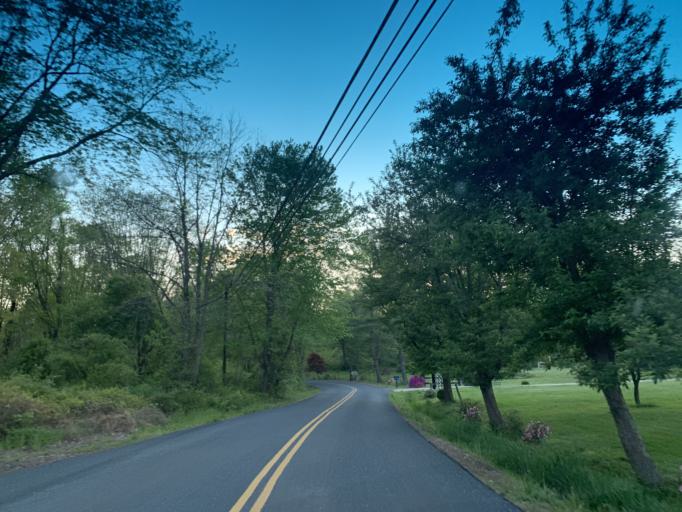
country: US
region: Maryland
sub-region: Harford County
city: Riverside
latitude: 39.5252
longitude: -76.2512
